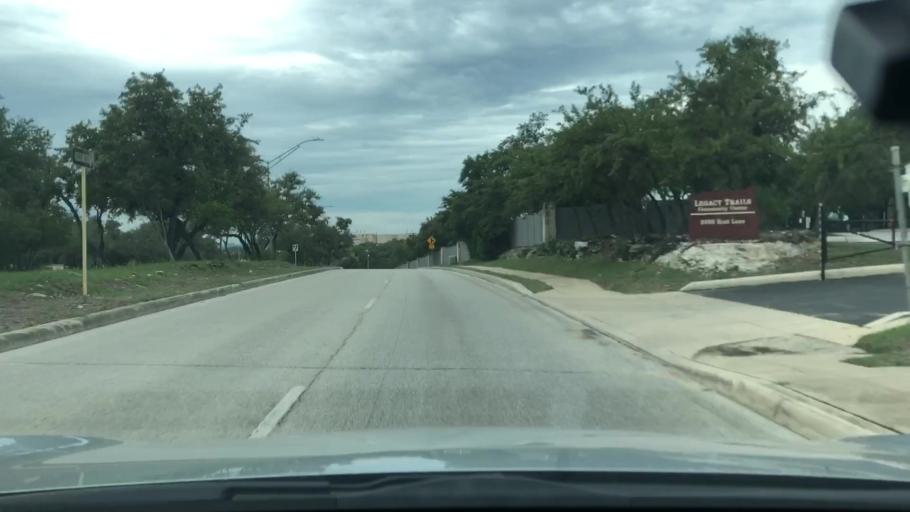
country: US
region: Texas
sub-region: Bexar County
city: Leon Valley
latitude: 29.4642
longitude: -98.6740
